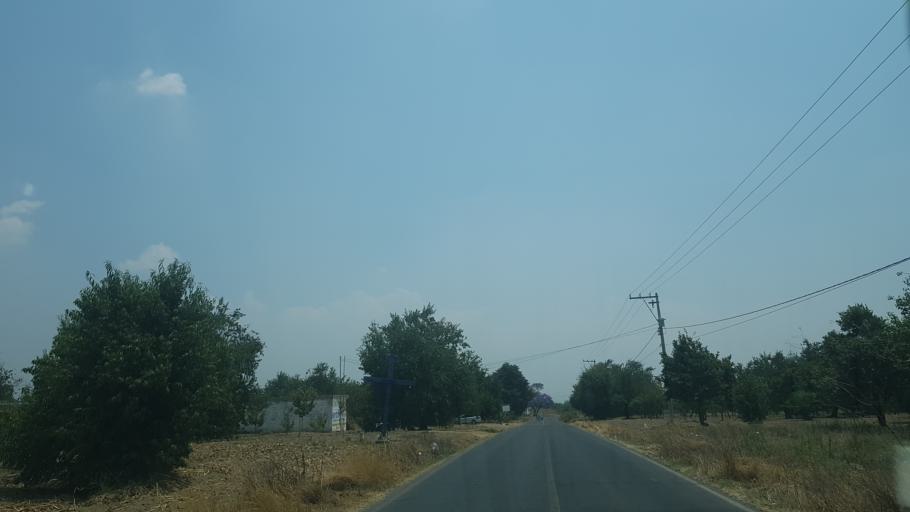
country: MX
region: Puebla
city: San Andres Calpan
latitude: 19.0982
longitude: -98.4223
